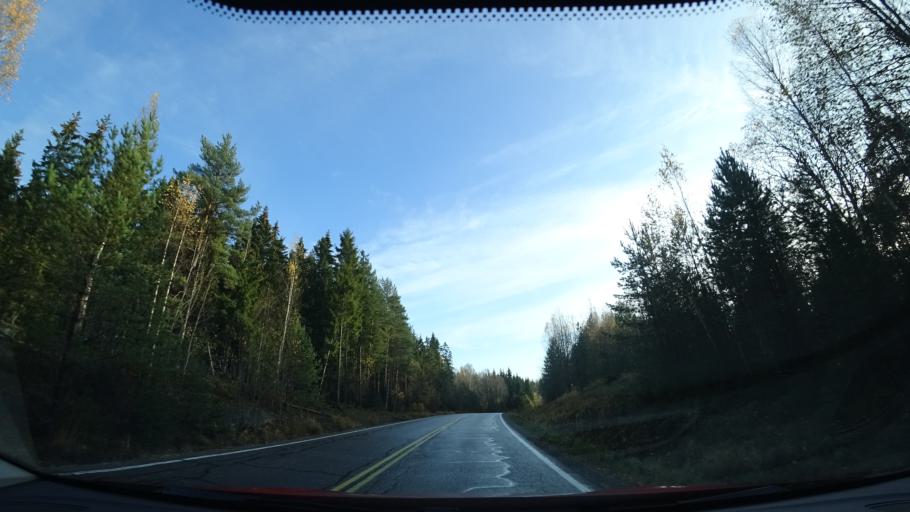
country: FI
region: Uusimaa
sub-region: Helsinki
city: Sibbo
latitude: 60.2759
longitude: 25.2015
